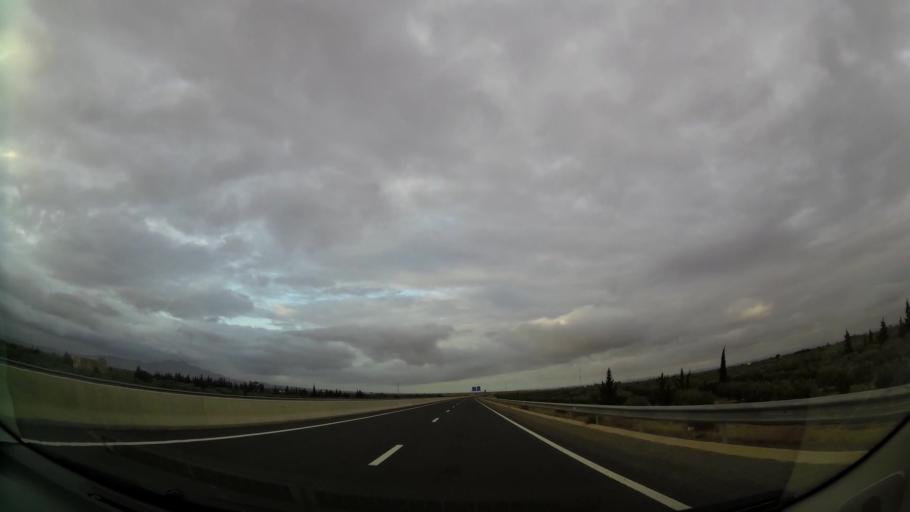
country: MA
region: Taza-Al Hoceima-Taounate
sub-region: Taza
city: Guercif
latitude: 34.3426
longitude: -3.3242
